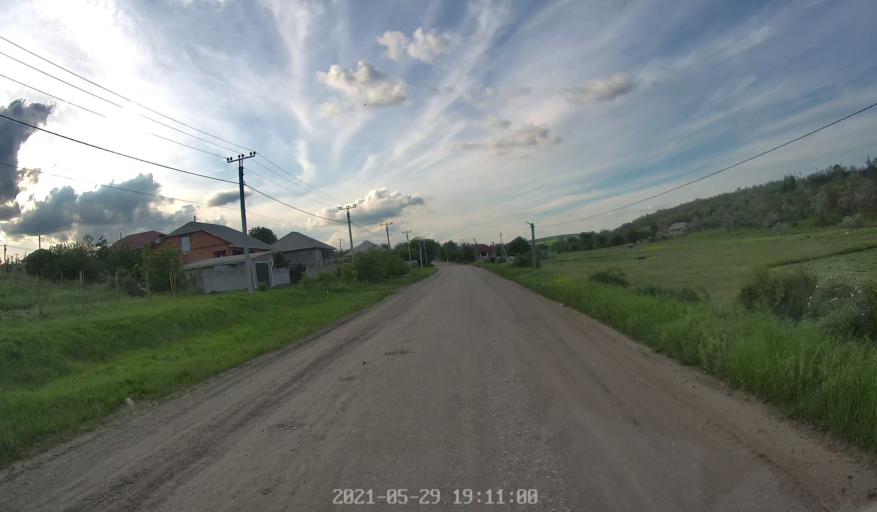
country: MD
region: Chisinau
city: Singera
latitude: 46.8356
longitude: 28.9554
